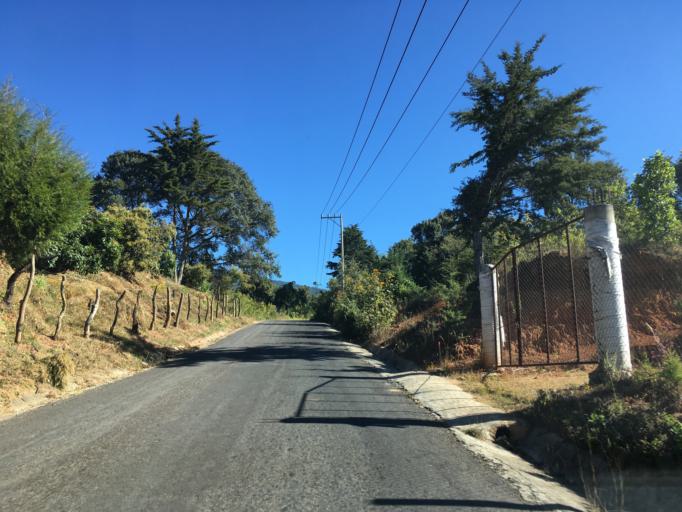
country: MX
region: Michoacan
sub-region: Zitacuaro
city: Valle Verde
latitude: 19.4831
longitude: -100.3324
